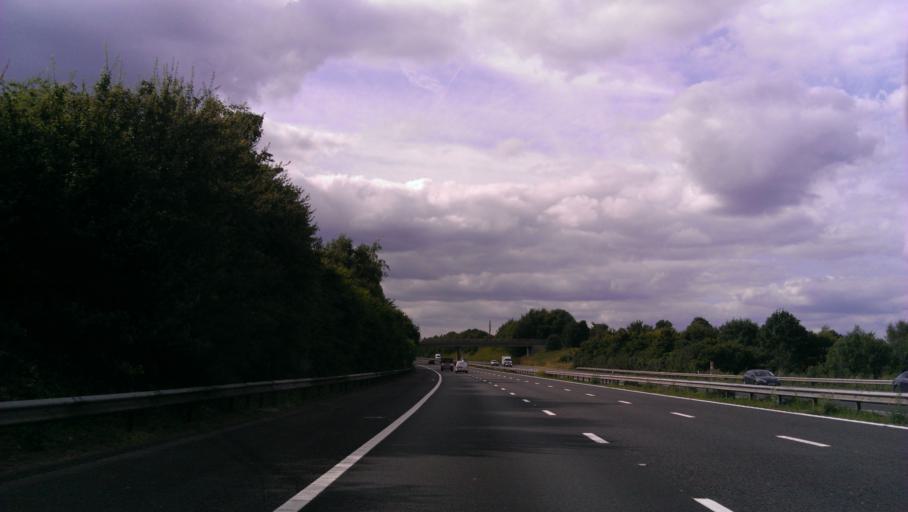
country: GB
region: England
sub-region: Kent
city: Longfield
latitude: 51.3610
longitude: 0.2678
